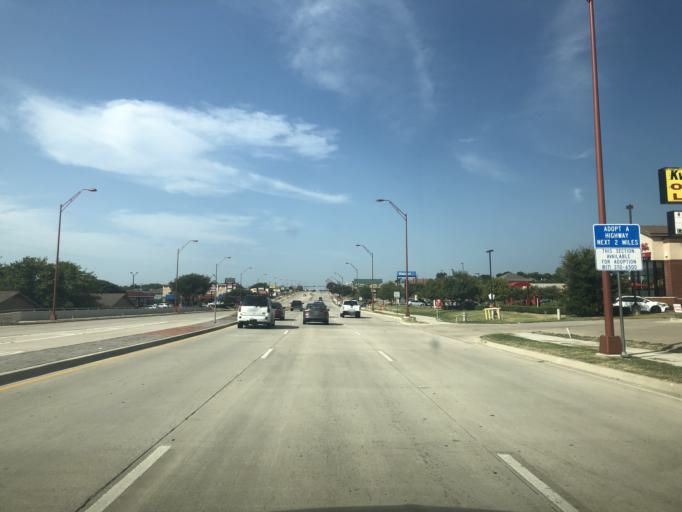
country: US
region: Texas
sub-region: Tarrant County
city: Benbrook
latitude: 32.6784
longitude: -97.4649
